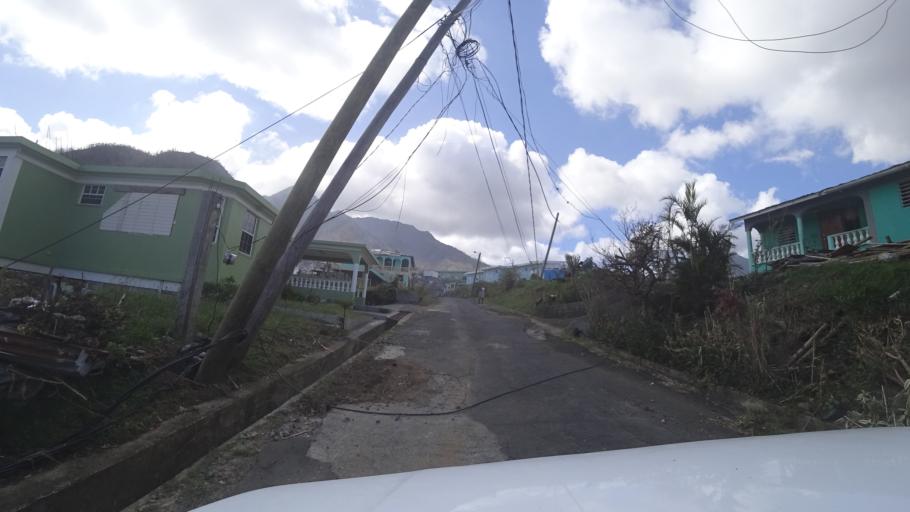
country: DM
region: Saint Patrick
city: Berekua
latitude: 15.2435
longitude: -61.3200
